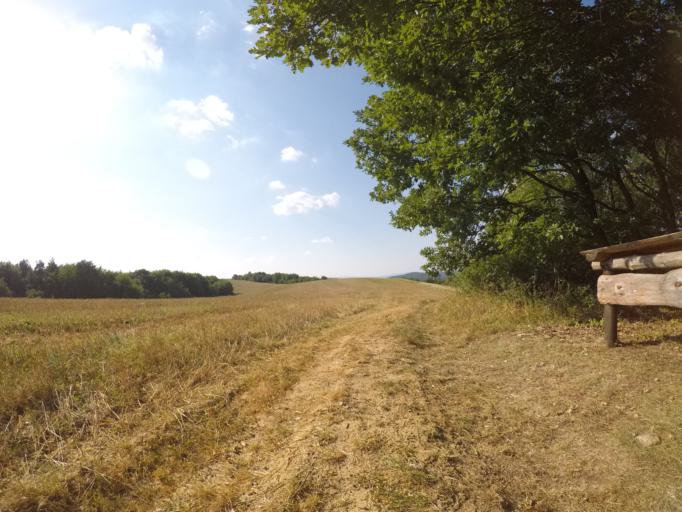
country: SK
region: Presovsky
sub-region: Okres Presov
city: Presov
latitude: 48.9355
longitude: 21.1693
